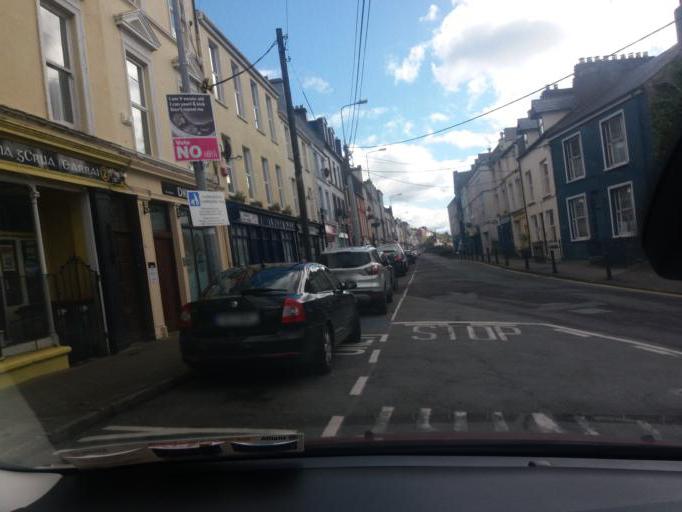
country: IE
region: Munster
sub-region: County Cork
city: Cobh
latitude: 51.8509
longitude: -8.2902
